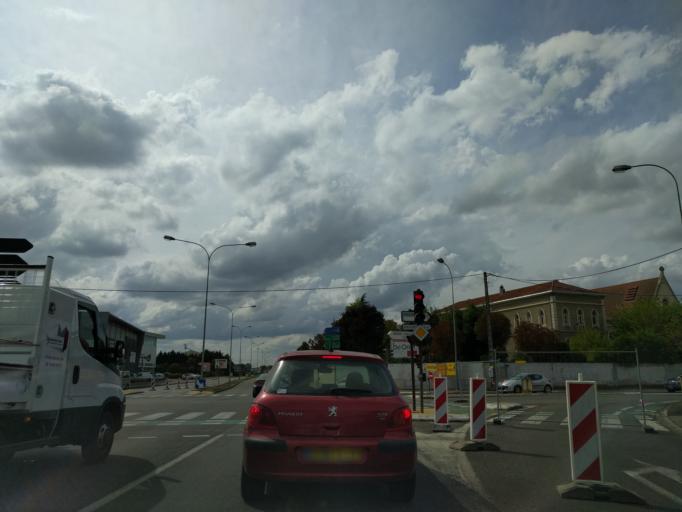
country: FR
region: Aquitaine
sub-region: Departement du Lot-et-Garonne
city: Agen
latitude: 44.1942
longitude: 0.6287
